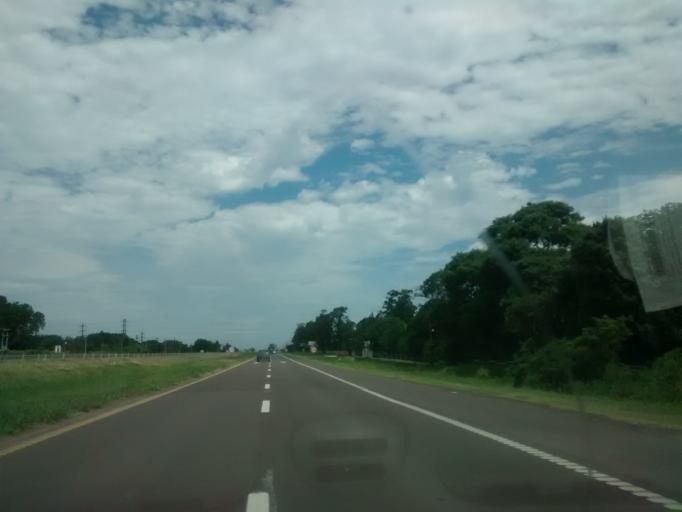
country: AR
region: Chaco
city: Fontana
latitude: -27.4029
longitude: -59.0126
